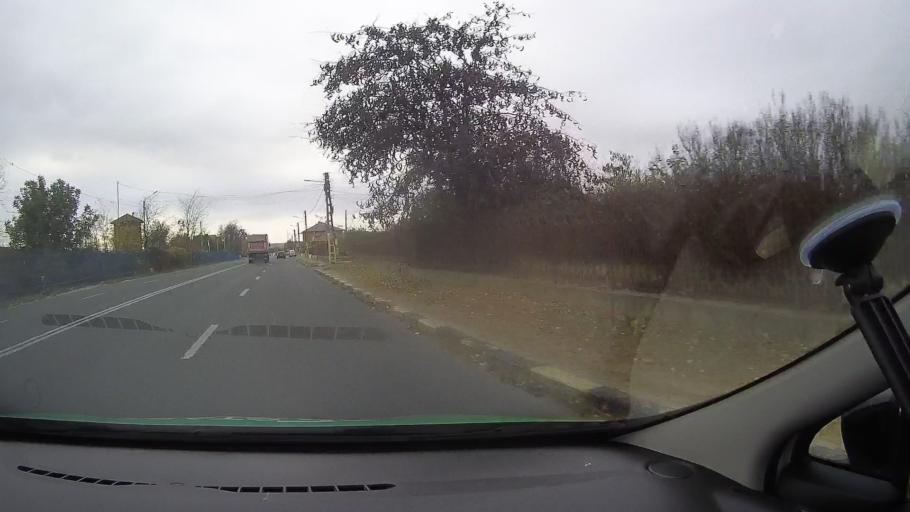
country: RO
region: Constanta
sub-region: Oras Murfatlar
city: Murfatlar
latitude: 44.1718
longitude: 28.4210
